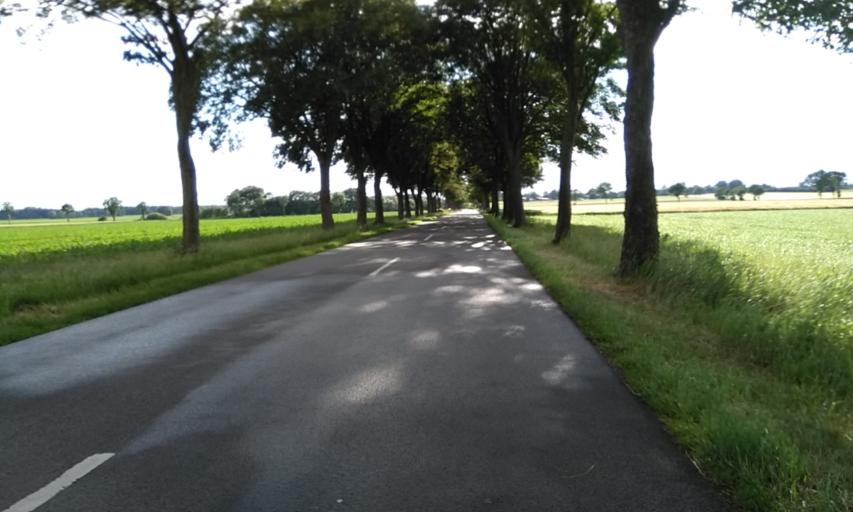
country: DE
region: Lower Saxony
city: Vierden
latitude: 53.3567
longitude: 9.4876
